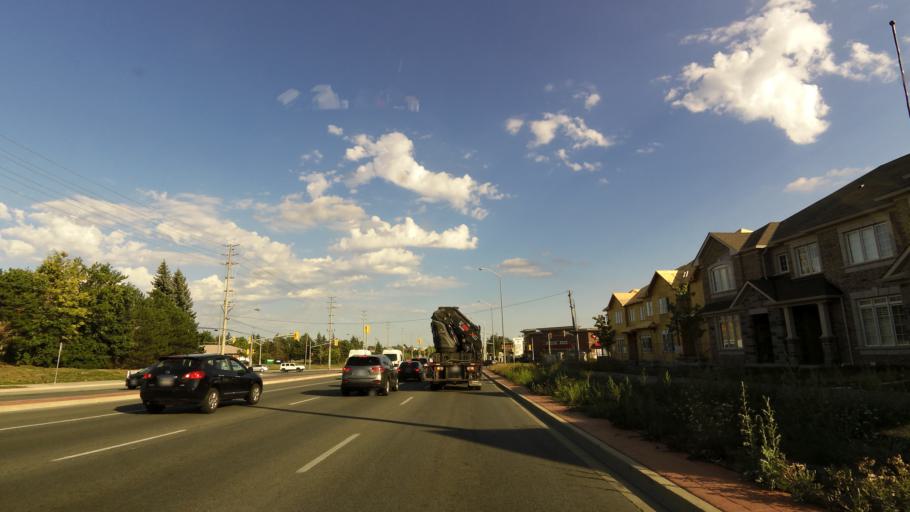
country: CA
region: Ontario
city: Brampton
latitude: 43.6568
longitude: -79.7685
